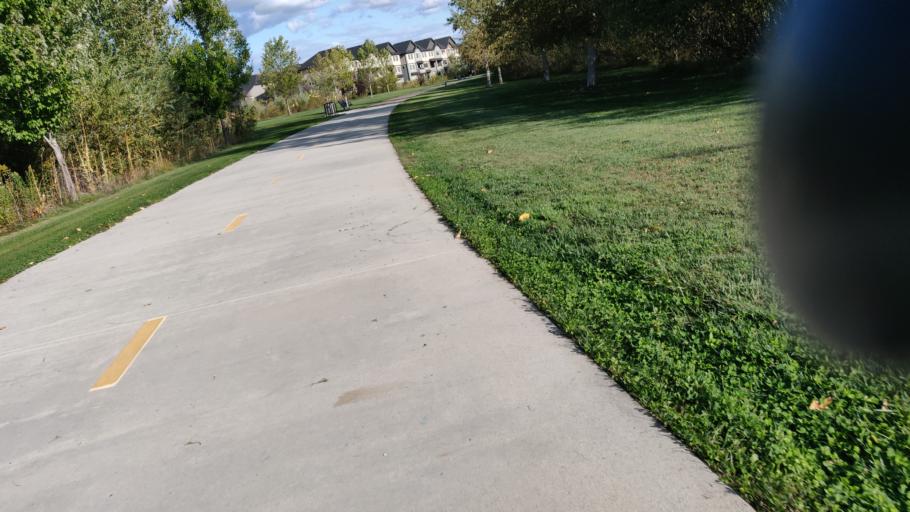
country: US
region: Idaho
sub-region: Ada County
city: Boise
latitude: 43.5751
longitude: -116.1477
